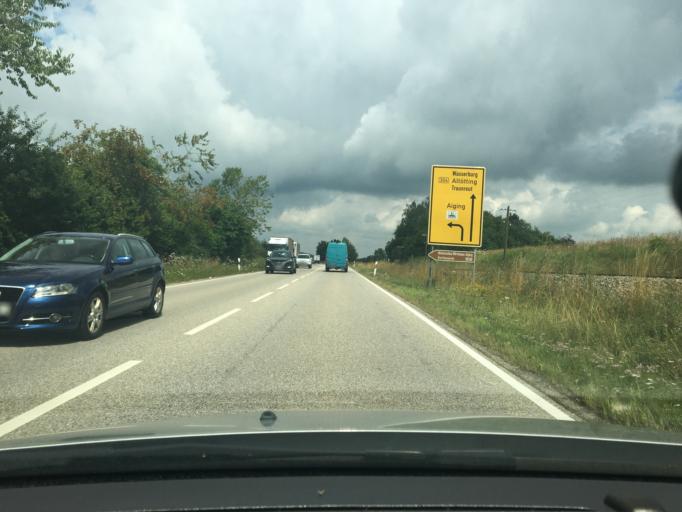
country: DE
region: Bavaria
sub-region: Upper Bavaria
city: Nussdorf
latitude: 47.9045
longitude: 12.6168
